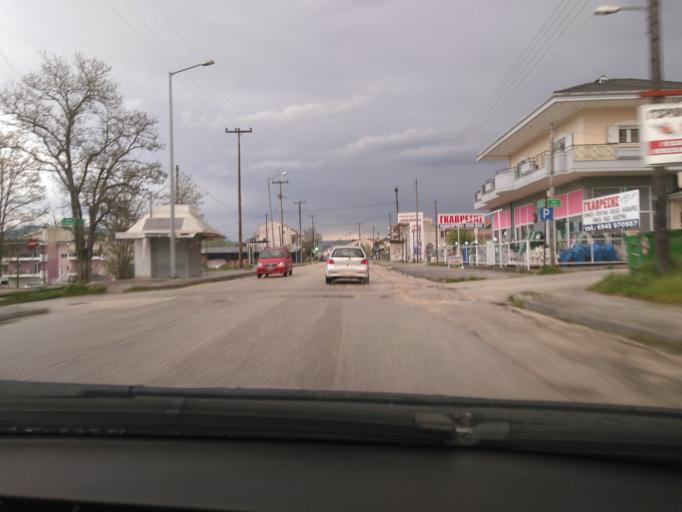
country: GR
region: Epirus
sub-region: Nomos Ioanninon
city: Anatoli
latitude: 39.6374
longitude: 20.8703
